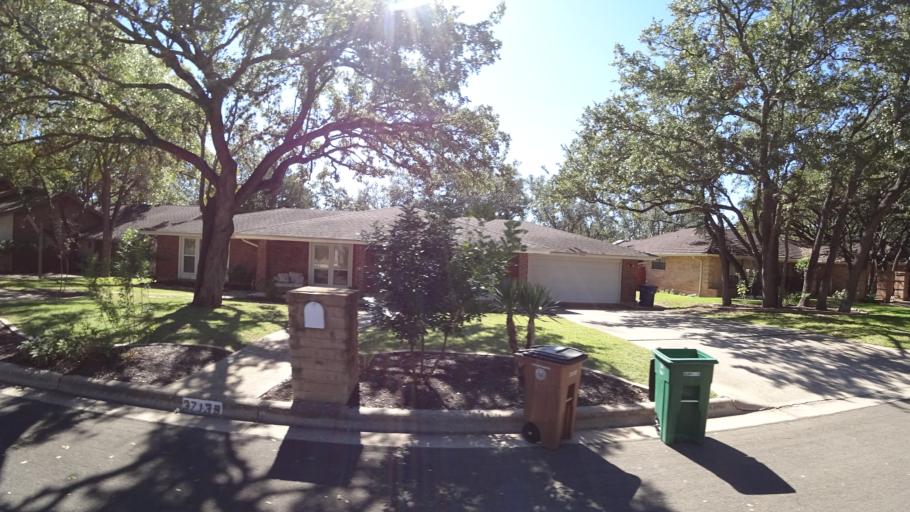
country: US
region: Texas
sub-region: Travis County
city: West Lake Hills
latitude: 30.3628
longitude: -97.7540
